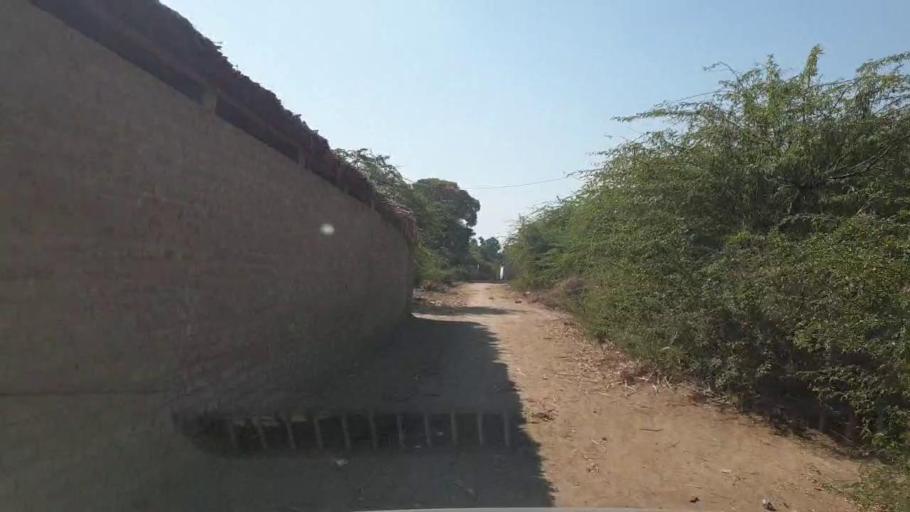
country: PK
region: Sindh
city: Digri
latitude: 25.2631
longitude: 69.2044
